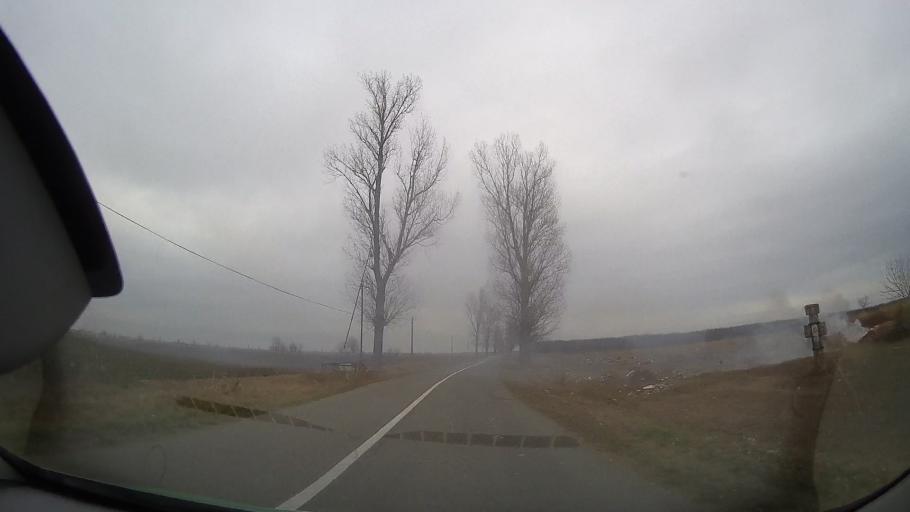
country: RO
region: Braila
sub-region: Comuna Rosiori
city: Rosiori
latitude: 44.8176
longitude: 27.3942
